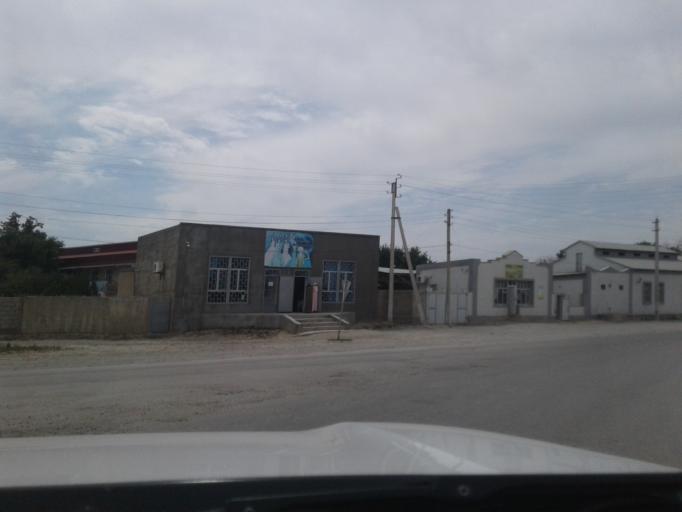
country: TM
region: Balkan
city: Serdar
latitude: 38.9881
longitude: 56.2819
